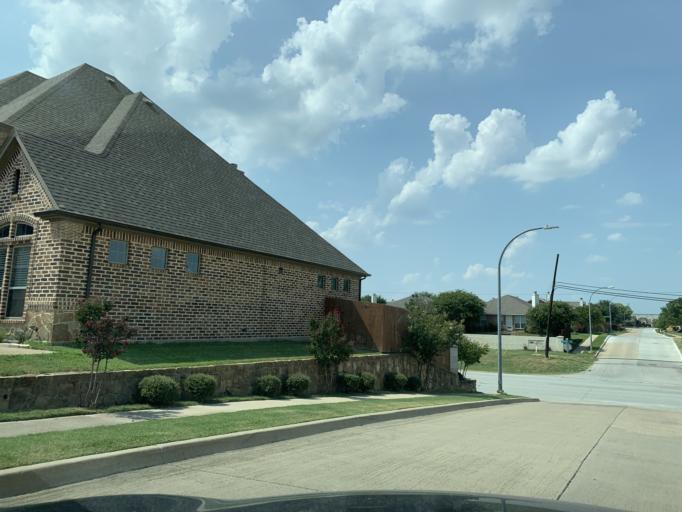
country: US
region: Texas
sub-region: Tarrant County
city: Richland Hills
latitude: 32.8023
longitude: -97.1977
